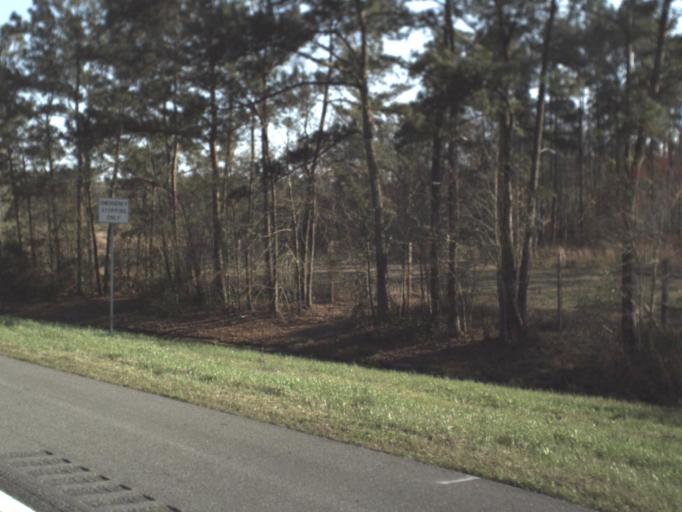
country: US
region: Florida
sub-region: Gadsden County
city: Midway
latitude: 30.5031
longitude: -84.4581
